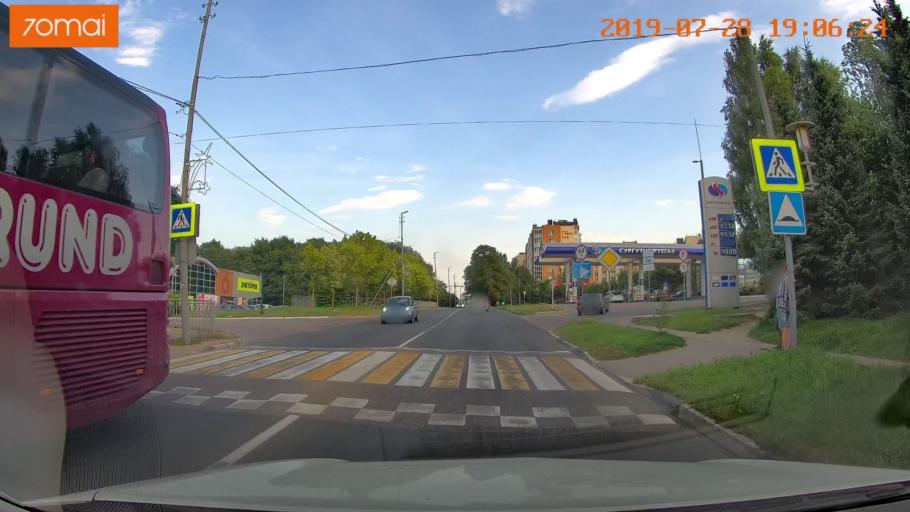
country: RU
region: Kaliningrad
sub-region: Gorod Svetlogorsk
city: Svetlogorsk
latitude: 54.9313
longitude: 20.1651
